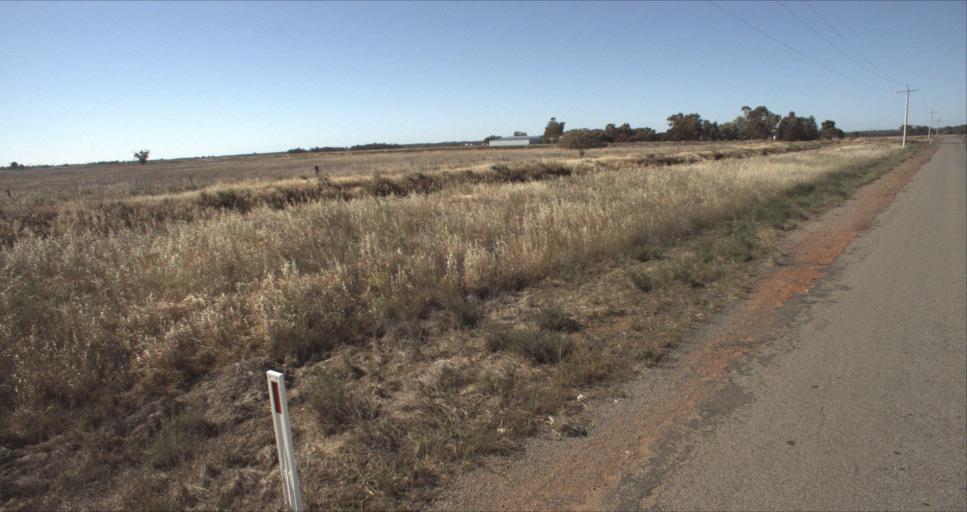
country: AU
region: New South Wales
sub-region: Leeton
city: Leeton
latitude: -34.5801
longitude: 146.3090
